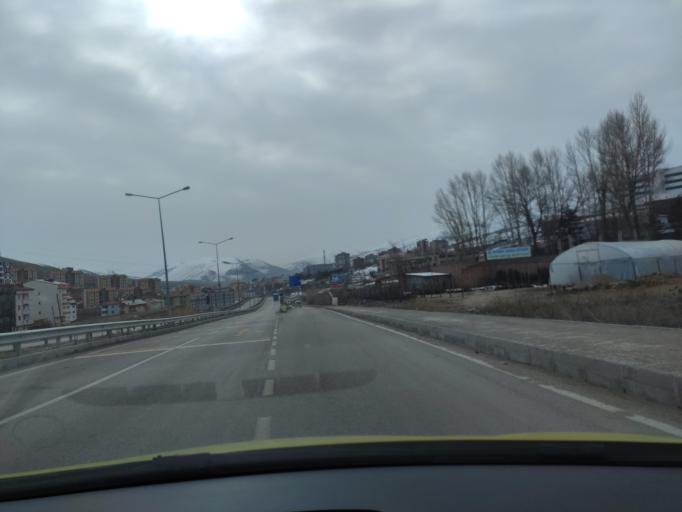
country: TR
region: Bayburt
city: Bayburt
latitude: 40.2617
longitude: 40.2091
